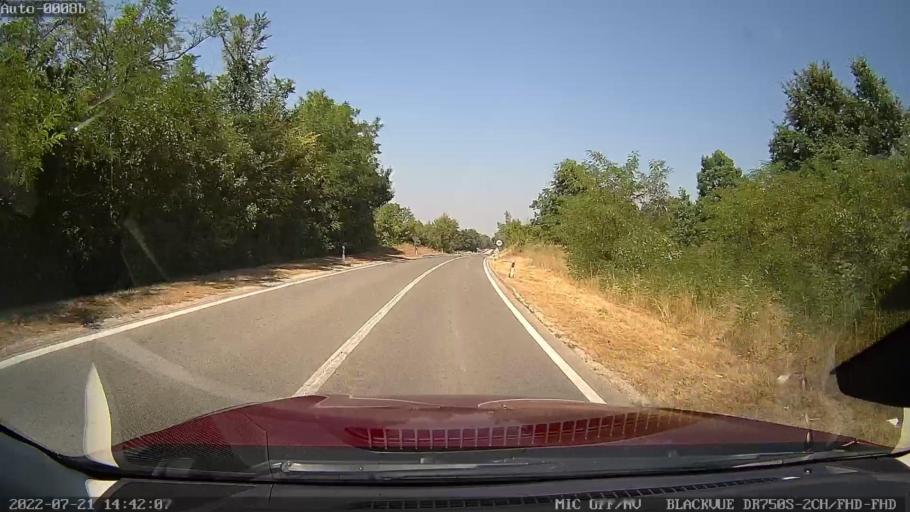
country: HR
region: Istarska
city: Vodnjan
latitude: 45.0951
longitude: 13.8808
